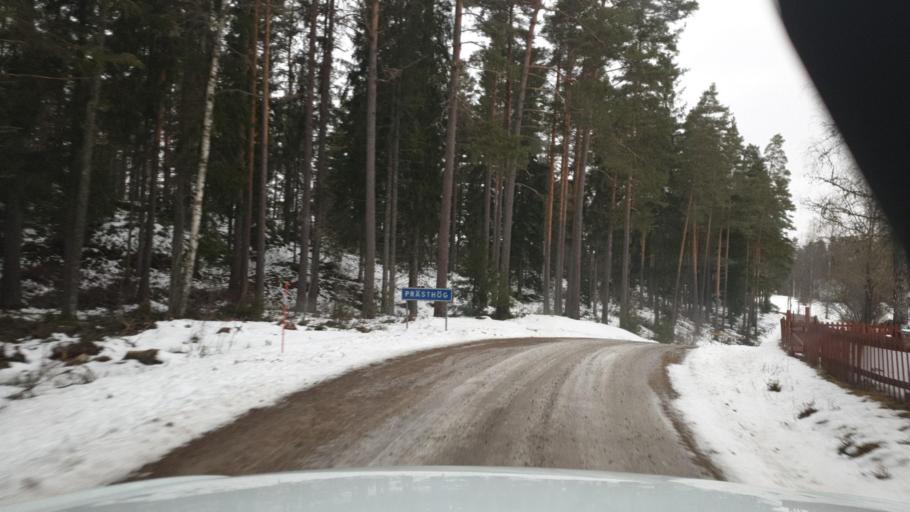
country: SE
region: Vaermland
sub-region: Arvika Kommun
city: Arvika
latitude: 59.5691
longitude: 12.7392
